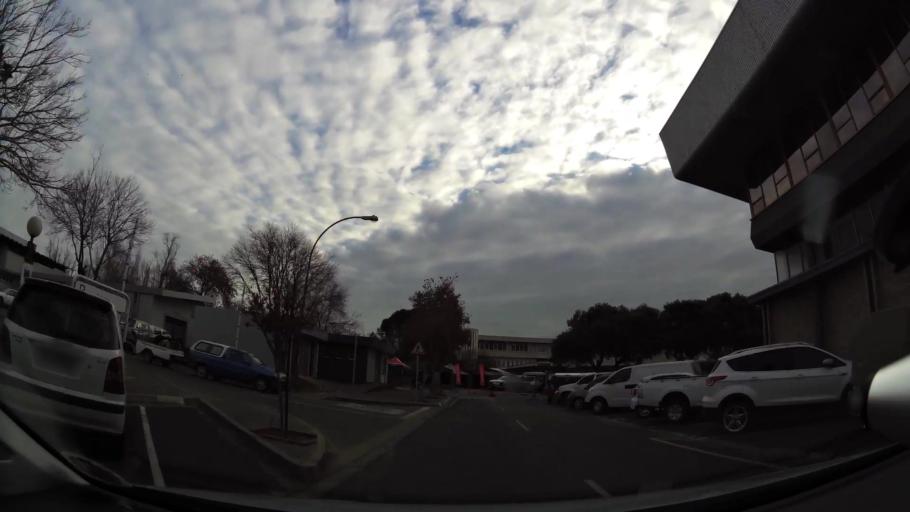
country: ZA
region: Orange Free State
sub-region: Mangaung Metropolitan Municipality
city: Bloemfontein
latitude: -29.1128
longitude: 26.1885
